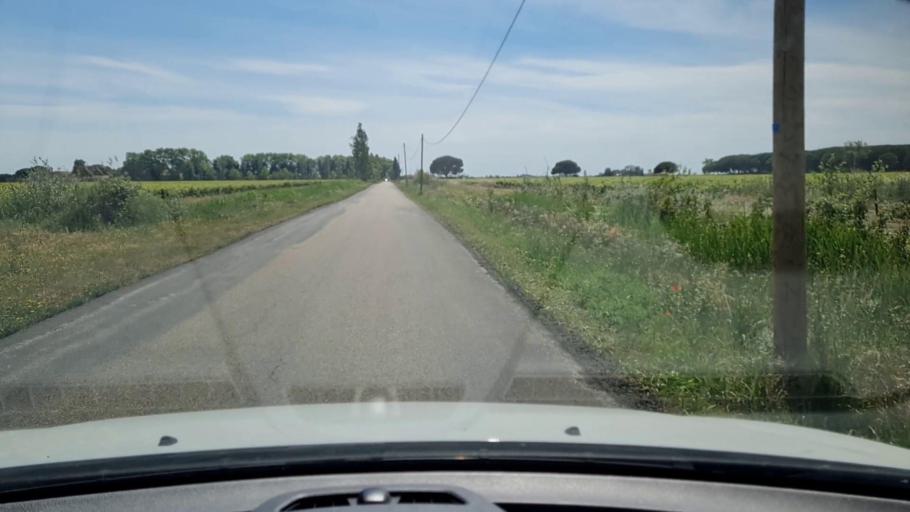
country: FR
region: Languedoc-Roussillon
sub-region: Departement du Gard
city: Vauvert
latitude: 43.5807
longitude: 4.3347
